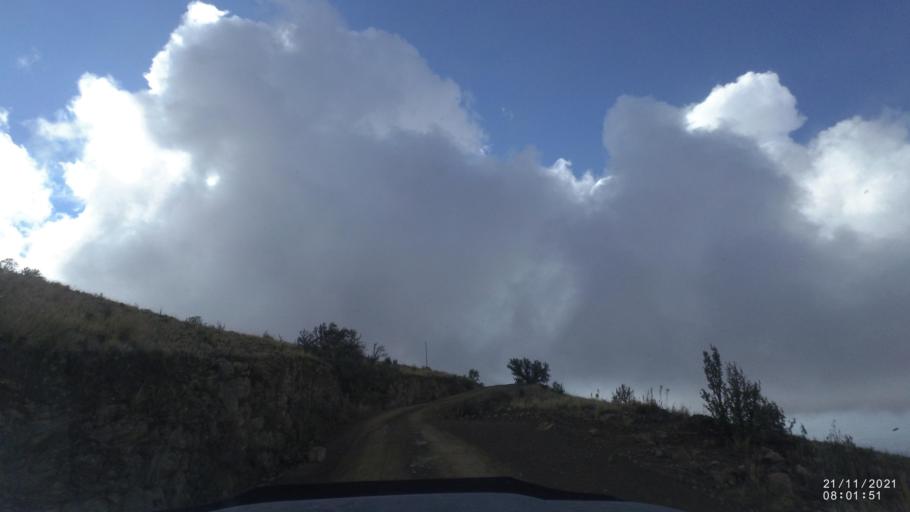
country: BO
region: Cochabamba
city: Cochabamba
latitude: -17.2882
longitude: -66.2190
